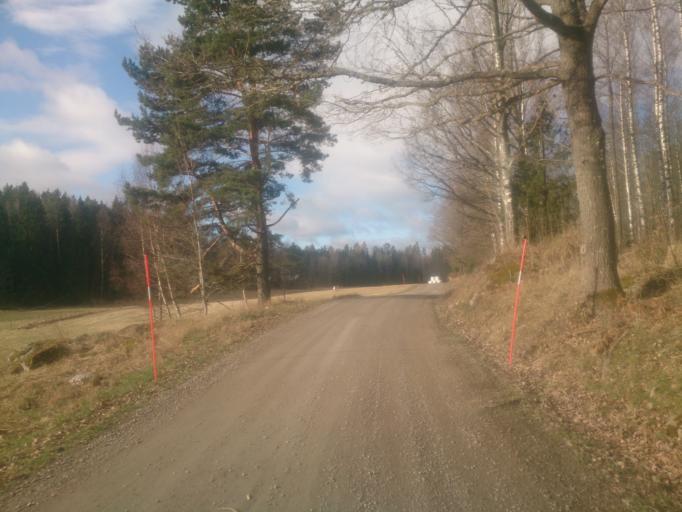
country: SE
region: OEstergoetland
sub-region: Atvidabergs Kommun
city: Atvidaberg
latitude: 58.2301
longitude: 16.1792
